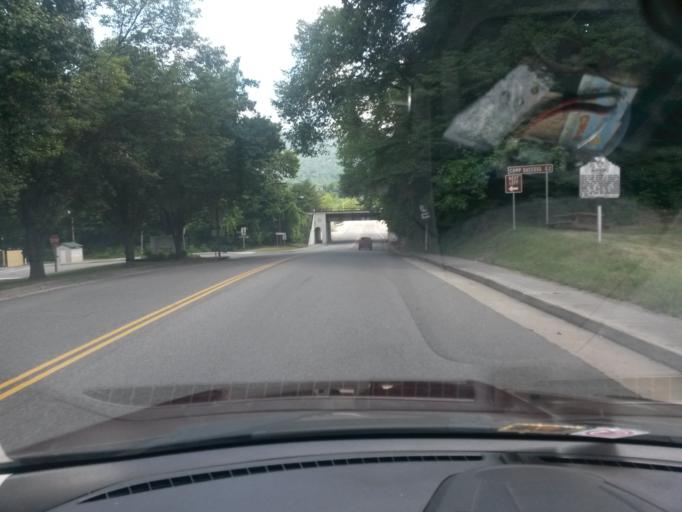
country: US
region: Virginia
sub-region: Giles County
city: Narrows
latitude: 37.3324
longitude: -80.8110
